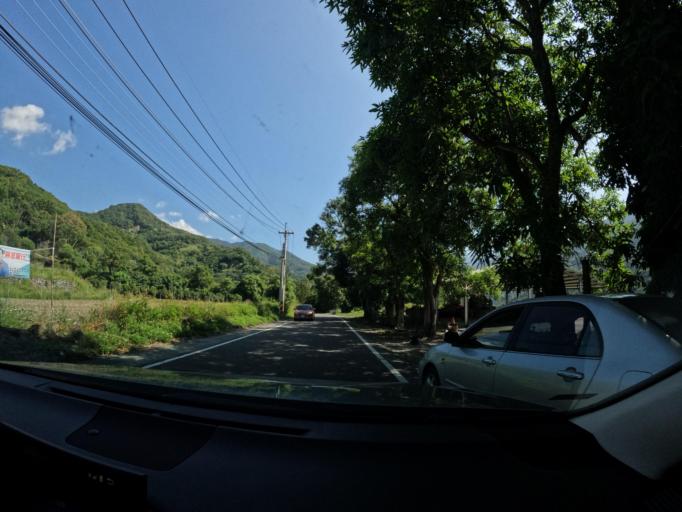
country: TW
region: Taiwan
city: Yujing
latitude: 23.1262
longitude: 120.7138
